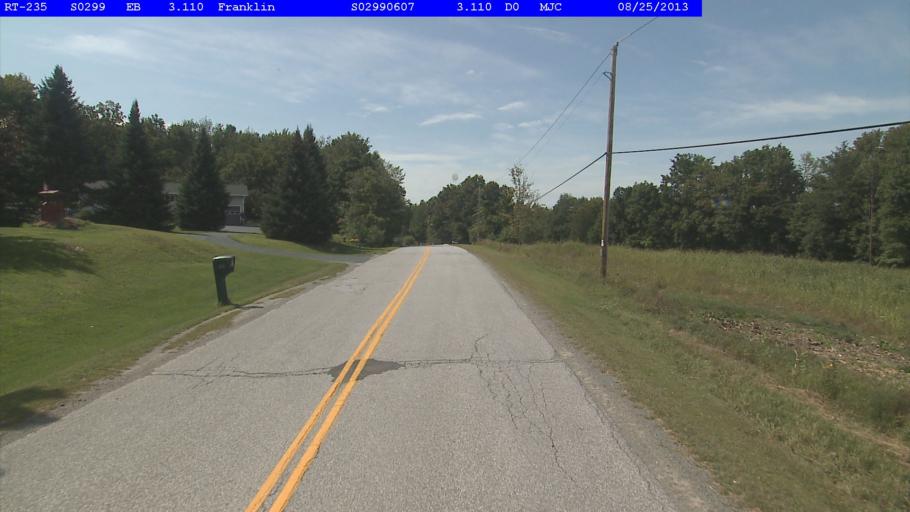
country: CA
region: Quebec
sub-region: Monteregie
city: Bedford
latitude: 45.0028
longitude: -72.9622
